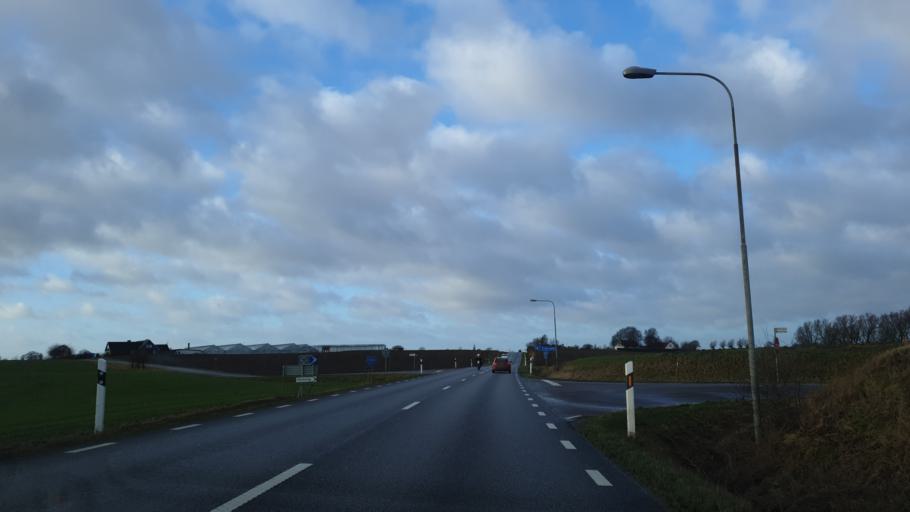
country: SE
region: Skane
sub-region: Trelleborgs Kommun
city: Trelleborg
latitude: 55.4558
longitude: 13.1713
